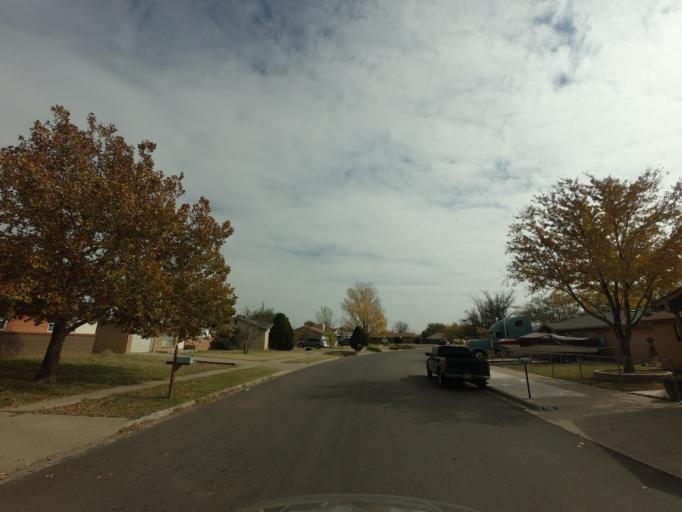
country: US
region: New Mexico
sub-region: Curry County
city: Clovis
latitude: 34.4314
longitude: -103.2193
